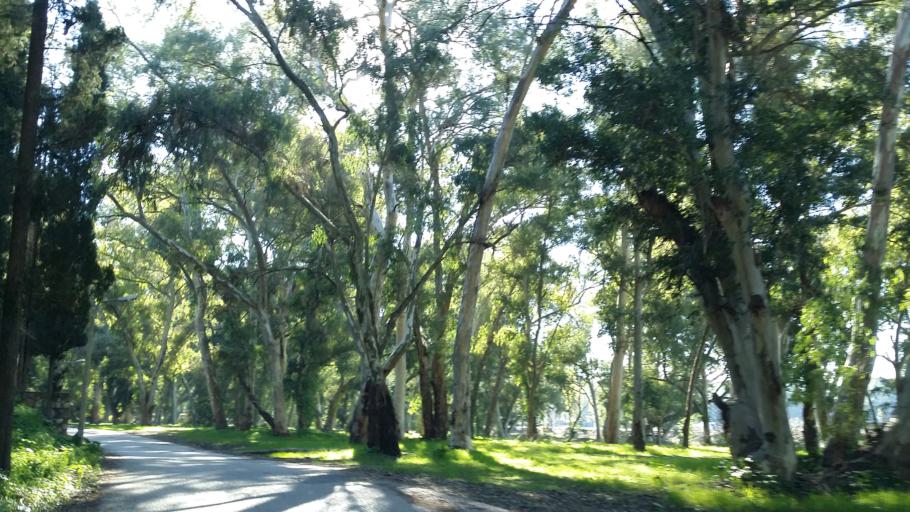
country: GR
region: West Greece
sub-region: Nomos Aitolias kai Akarnanias
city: Vonitsa
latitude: 38.9222
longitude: 20.8817
